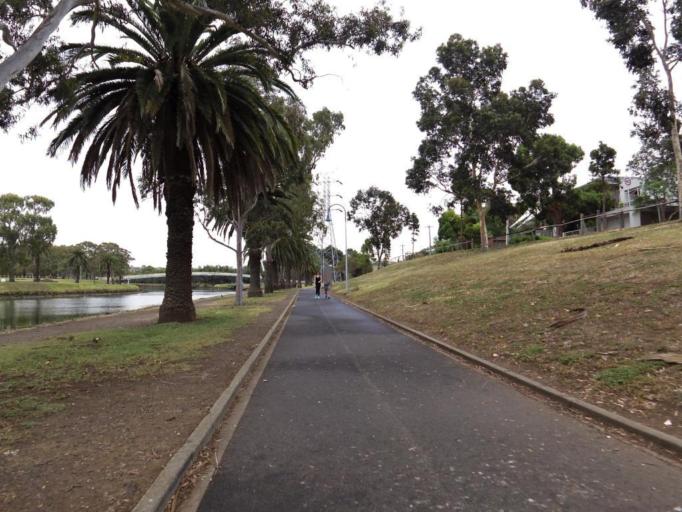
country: AU
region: Victoria
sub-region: Moonee Valley
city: Essendon West
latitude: -37.7631
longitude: 144.8912
